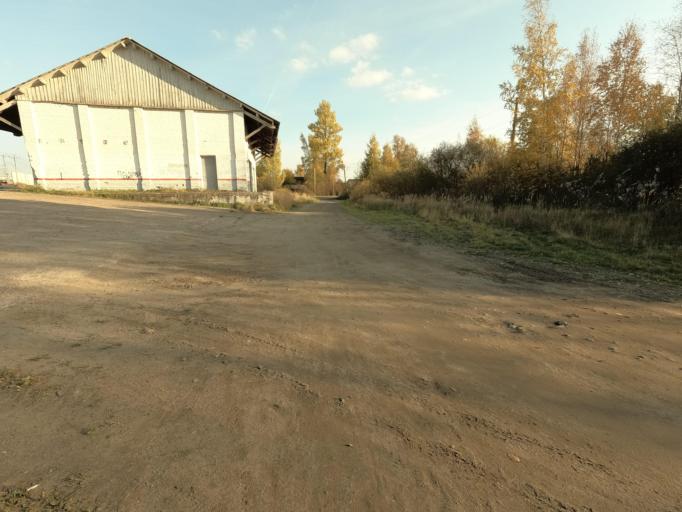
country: RU
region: Leningrad
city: Mga
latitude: 59.7555
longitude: 31.0548
